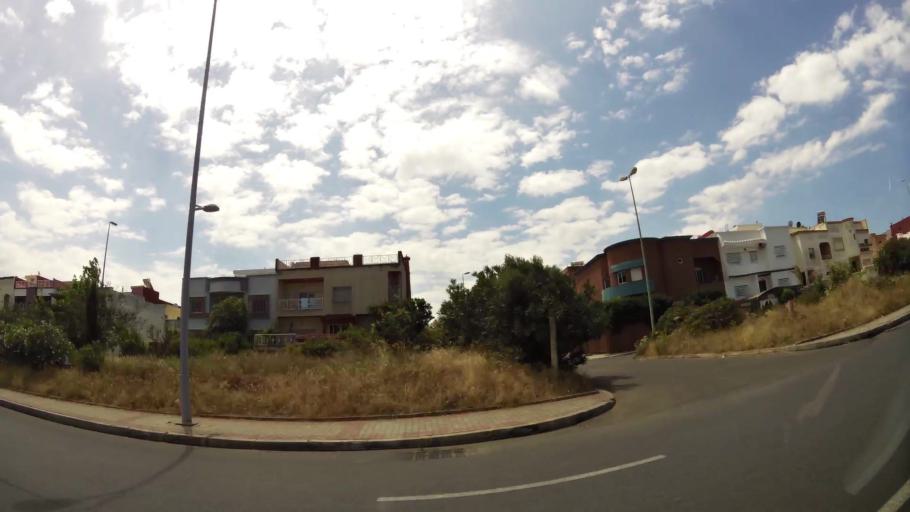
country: MA
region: Gharb-Chrarda-Beni Hssen
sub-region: Kenitra Province
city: Kenitra
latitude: 34.2770
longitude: -6.6084
